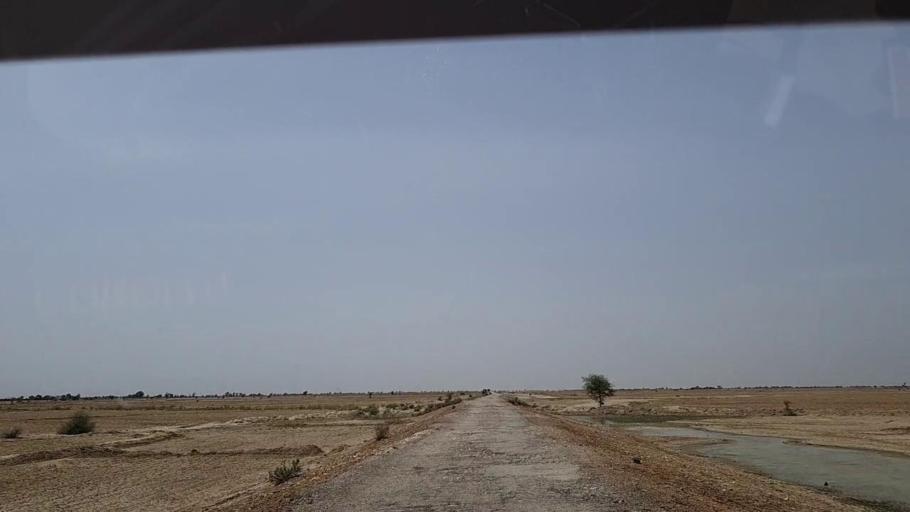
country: PK
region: Sindh
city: Johi
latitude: 26.7206
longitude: 67.6454
